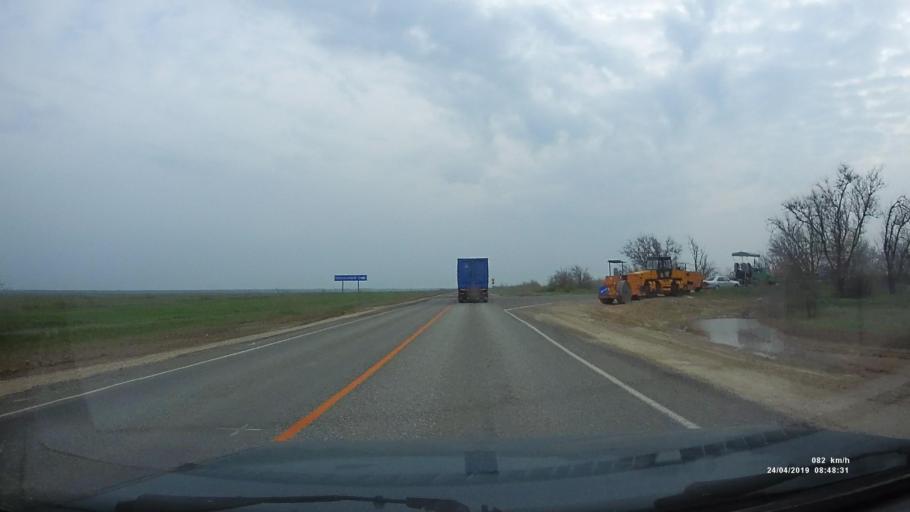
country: RU
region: Kalmykiya
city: Arshan'
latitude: 46.2514
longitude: 44.1099
